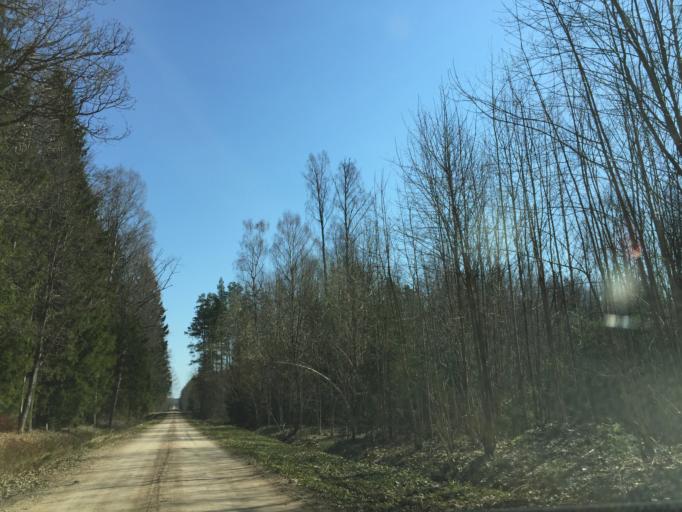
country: EE
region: Tartu
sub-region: Tartu linn
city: Tartu
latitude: 58.5284
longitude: 26.8942
